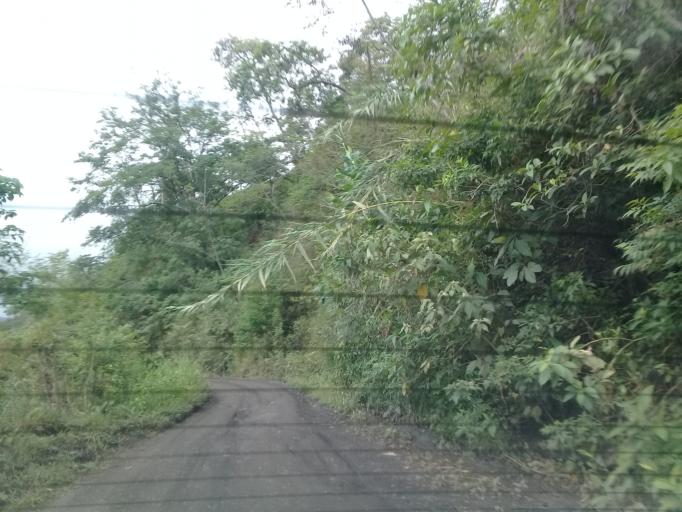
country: CO
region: Cundinamarca
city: Quipile
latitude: 4.7330
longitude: -74.5352
